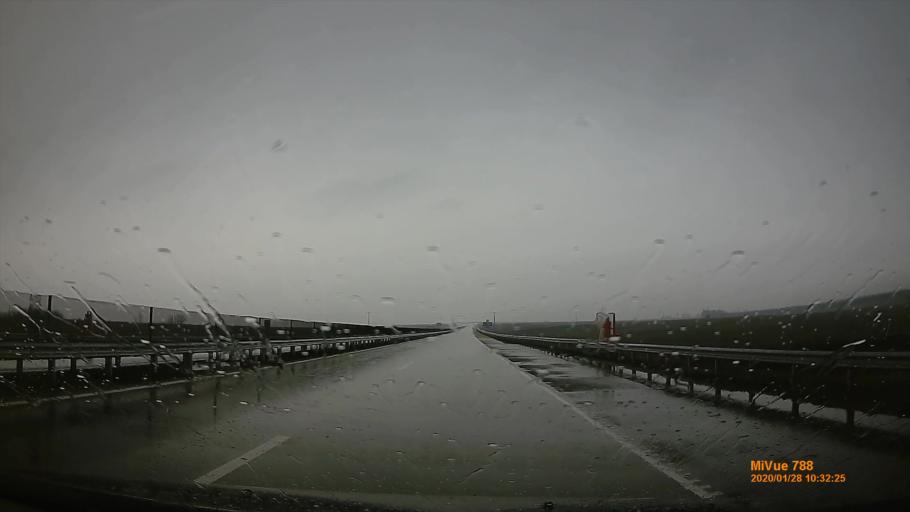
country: HU
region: Pest
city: Gomba
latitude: 47.3490
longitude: 19.4932
